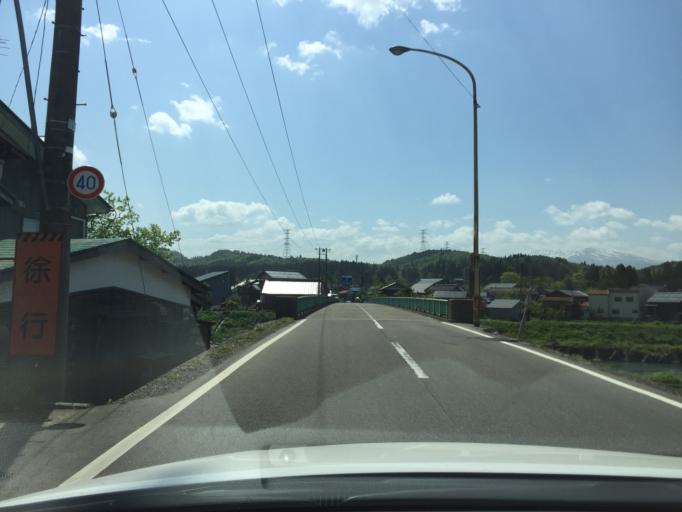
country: JP
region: Niigata
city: Tochio-honcho
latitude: 37.5466
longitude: 139.0903
